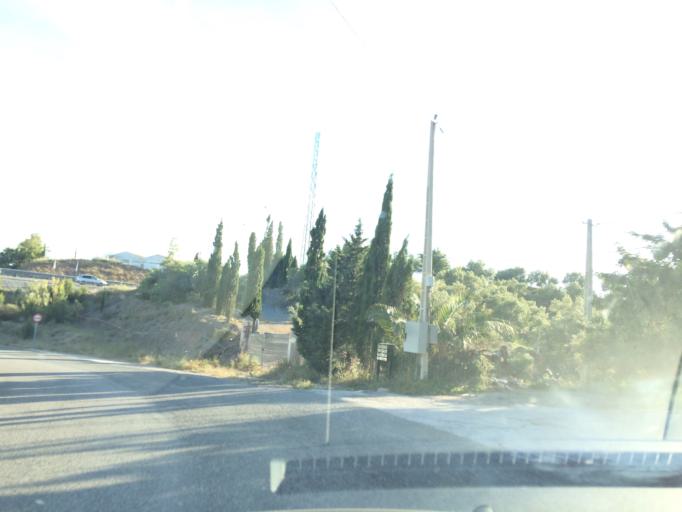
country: ES
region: Andalusia
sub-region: Provincia de Malaga
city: Totalan
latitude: 36.7336
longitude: -4.3392
